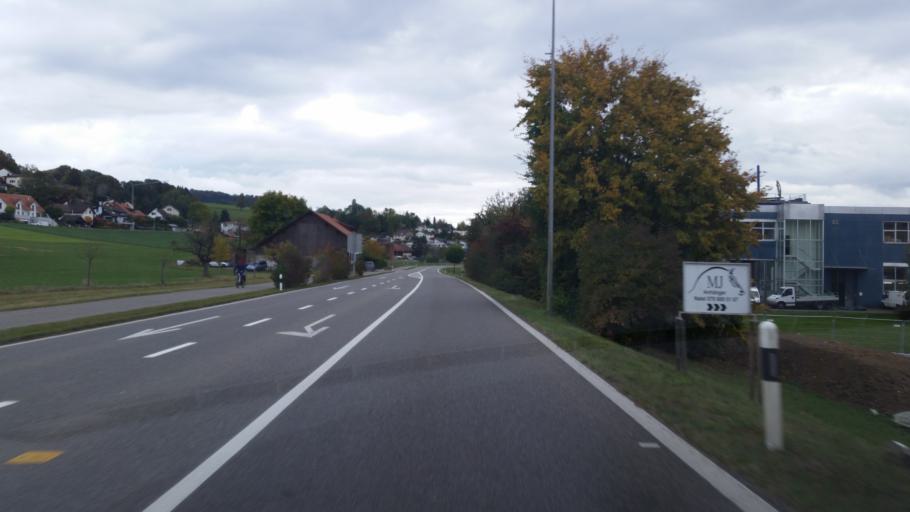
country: CH
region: Aargau
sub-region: Bezirk Zurzach
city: Oberendingen
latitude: 47.5283
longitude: 8.3191
